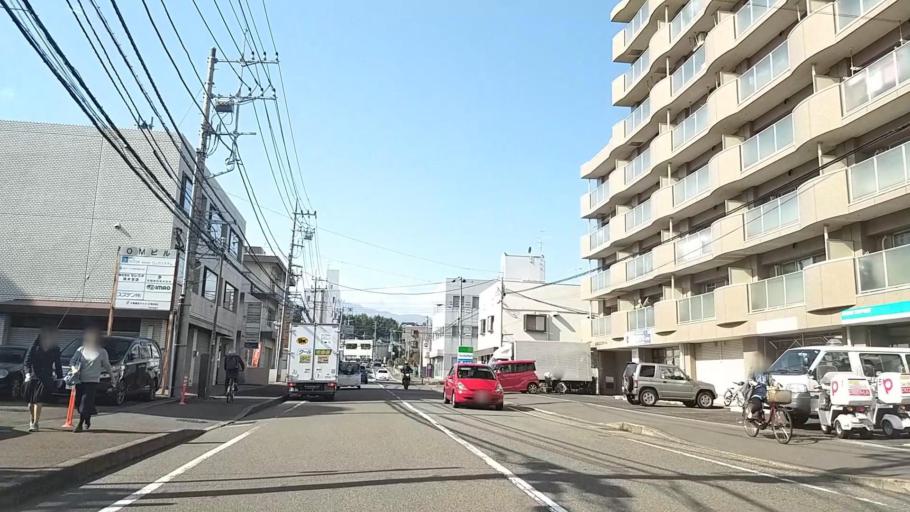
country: JP
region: Kanagawa
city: Atsugi
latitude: 35.4396
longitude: 139.3560
